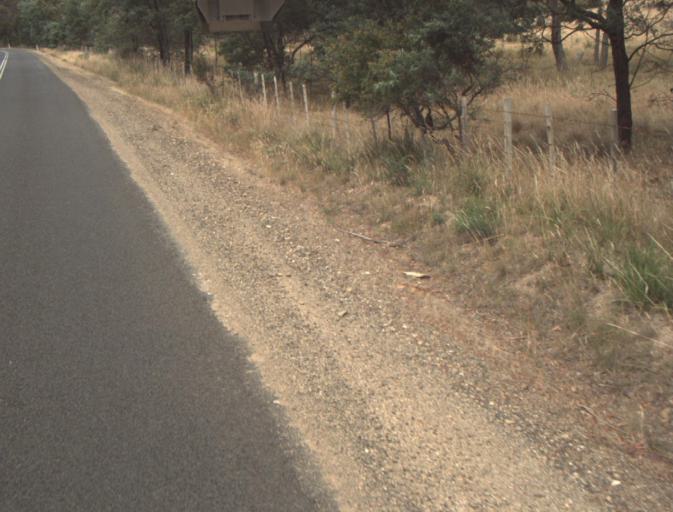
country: AU
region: Tasmania
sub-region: Northern Midlands
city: Evandale
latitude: -41.5123
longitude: 147.3328
